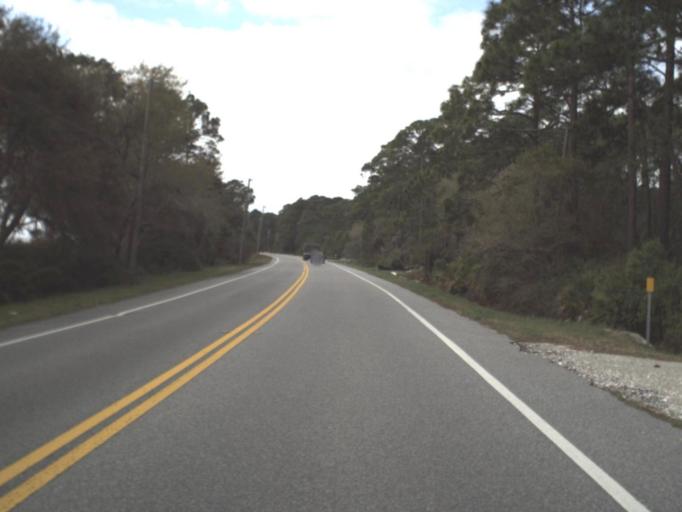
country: US
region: Florida
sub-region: Franklin County
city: Eastpoint
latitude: 29.7682
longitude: -84.8038
